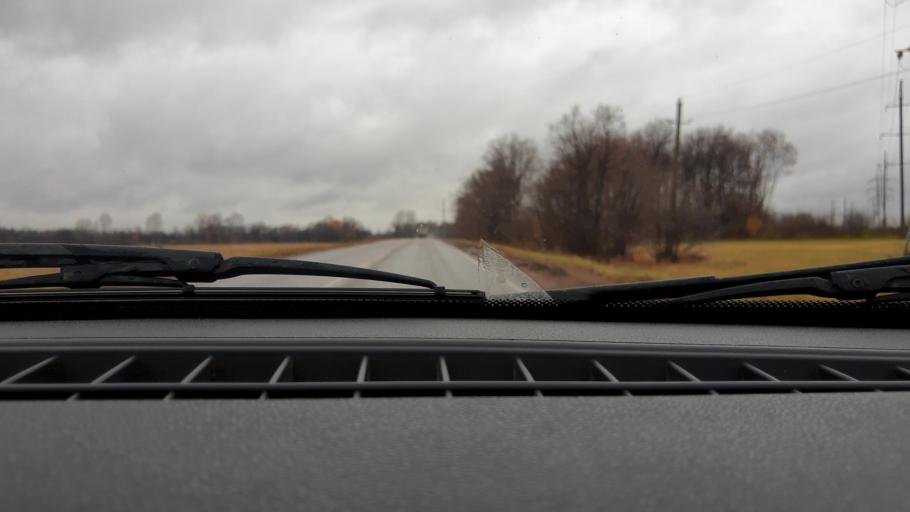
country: RU
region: Bashkortostan
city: Mikhaylovka
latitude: 54.8336
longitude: 55.7904
